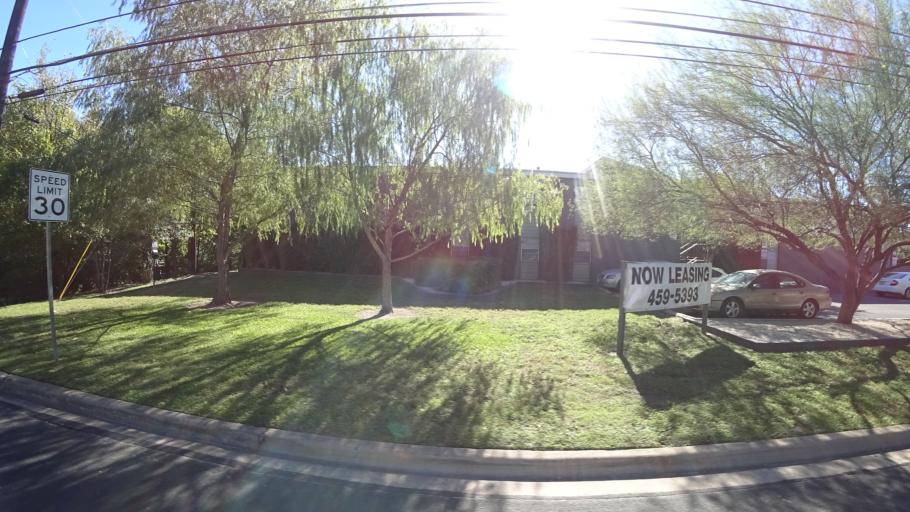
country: US
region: Texas
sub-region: Travis County
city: Austin
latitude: 30.3273
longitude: -97.7365
